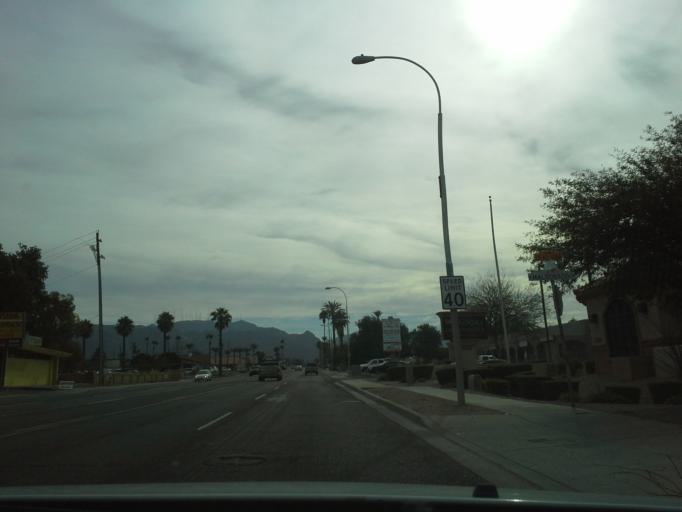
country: US
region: Arizona
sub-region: Maricopa County
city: Phoenix
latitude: 33.3838
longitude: -112.0734
